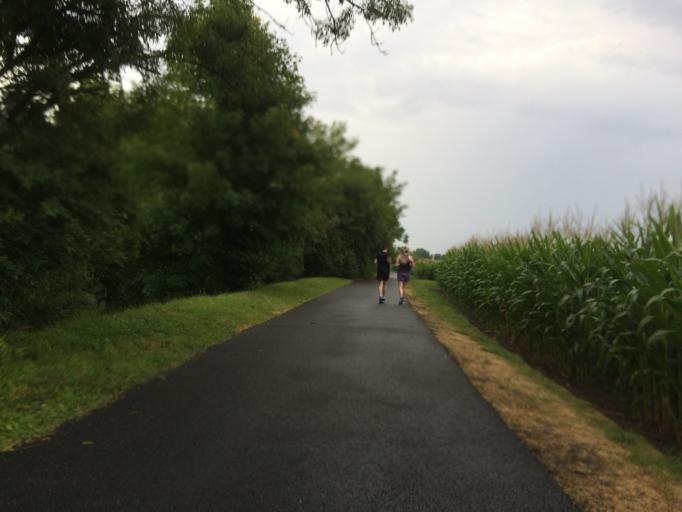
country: FR
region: Picardie
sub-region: Departement de l'Oise
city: Jaux
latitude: 49.3804
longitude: 2.7777
